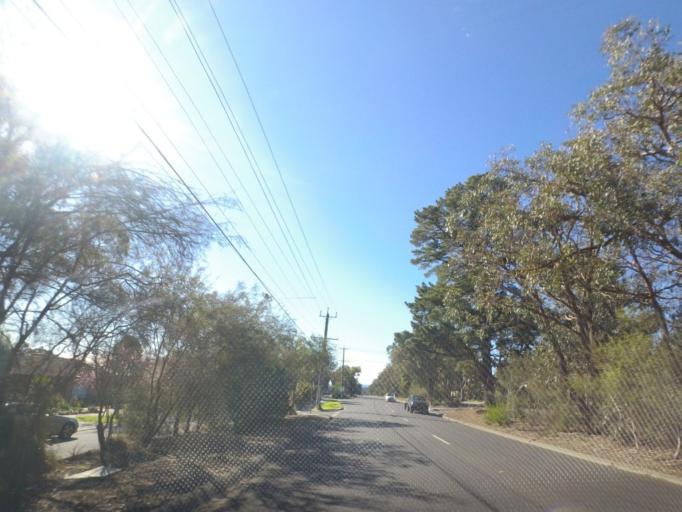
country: AU
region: Victoria
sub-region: Maroondah
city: Croydon Hills
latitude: -37.7787
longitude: 145.2748
